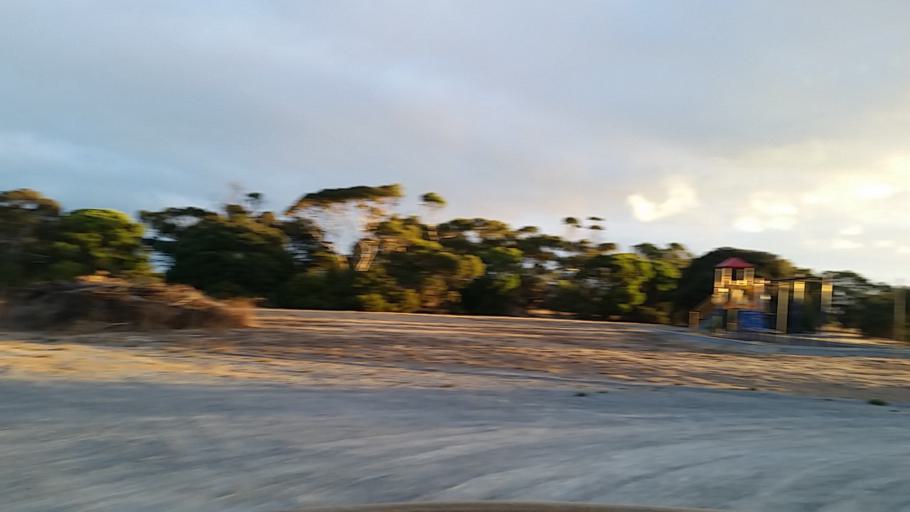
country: AU
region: South Australia
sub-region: Yankalilla
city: Normanville
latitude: -35.6061
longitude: 138.1091
